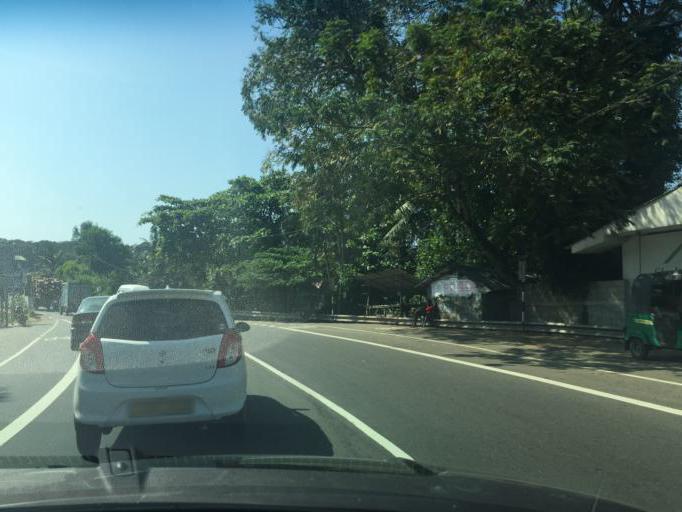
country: LK
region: Western
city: Moratuwa
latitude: 6.7950
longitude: 79.9055
